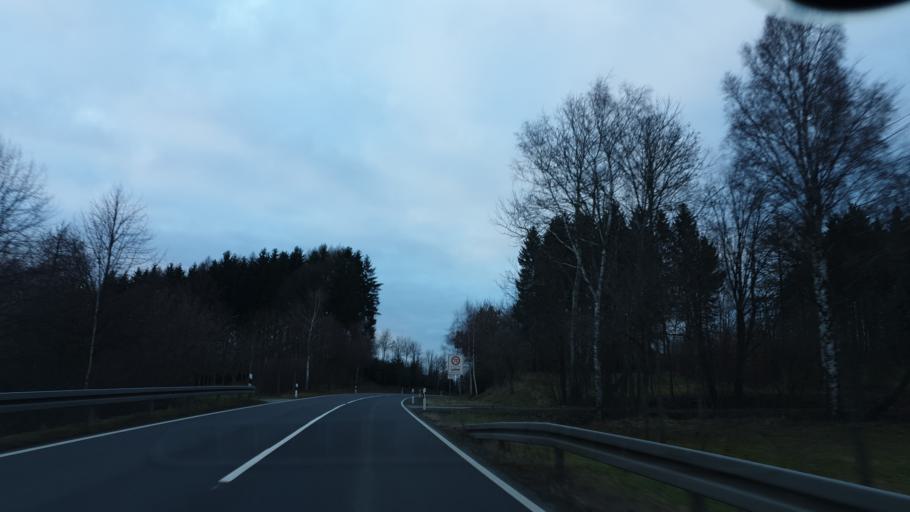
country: DE
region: Saxony
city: Elterlein
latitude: 50.5801
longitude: 12.8809
